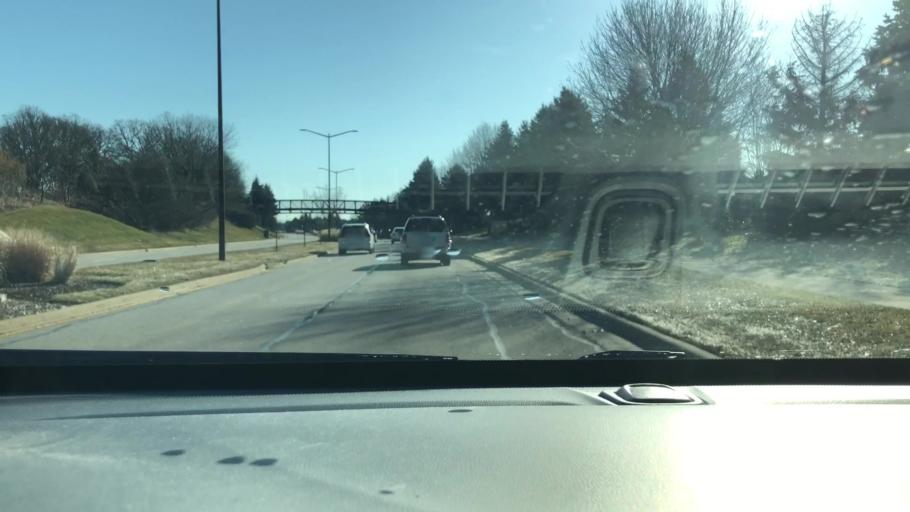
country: US
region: Illinois
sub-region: Kane County
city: Aurora
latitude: 41.7813
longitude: -88.2548
